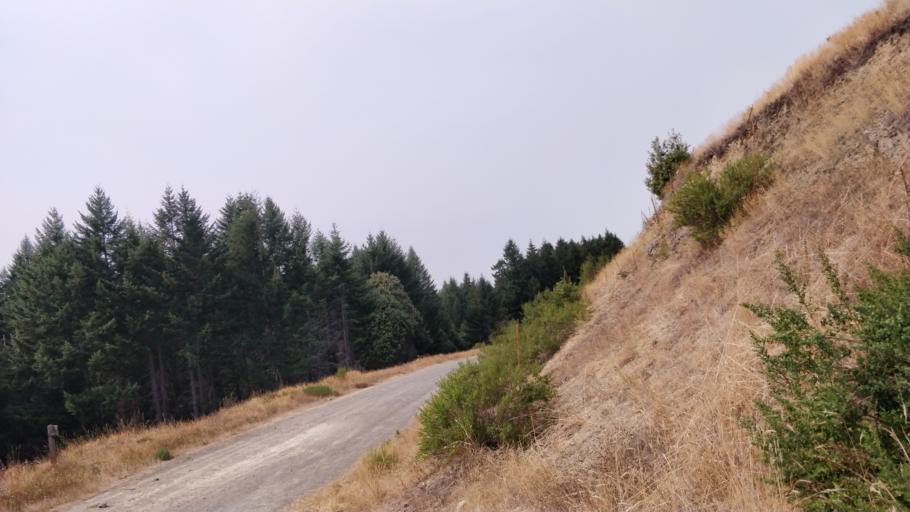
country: US
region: California
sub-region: Humboldt County
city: Westhaven-Moonstone
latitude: 41.2033
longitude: -123.9520
